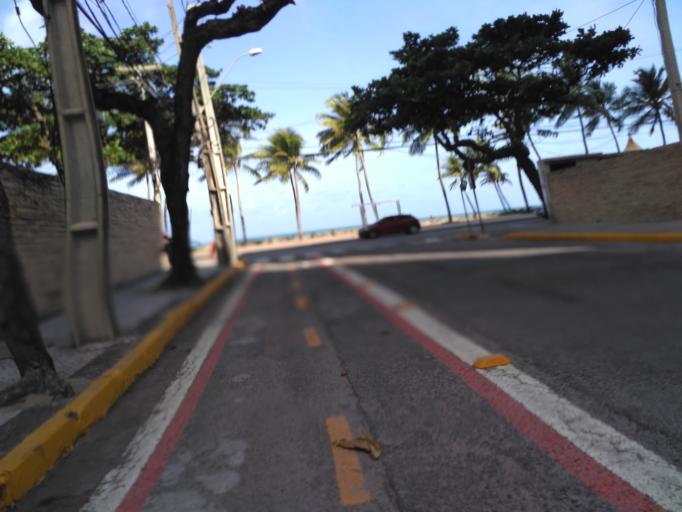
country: BR
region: Pernambuco
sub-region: Recife
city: Recife
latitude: -8.1439
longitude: -34.9049
